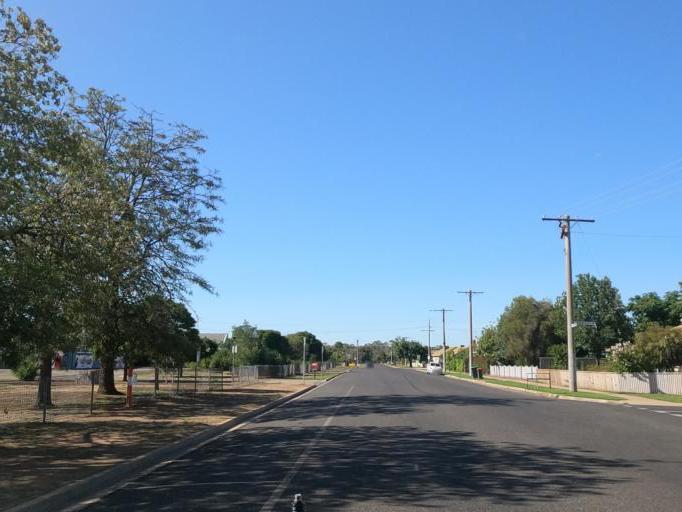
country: AU
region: Victoria
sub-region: Moira
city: Yarrawonga
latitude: -36.0208
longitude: 146.0054
